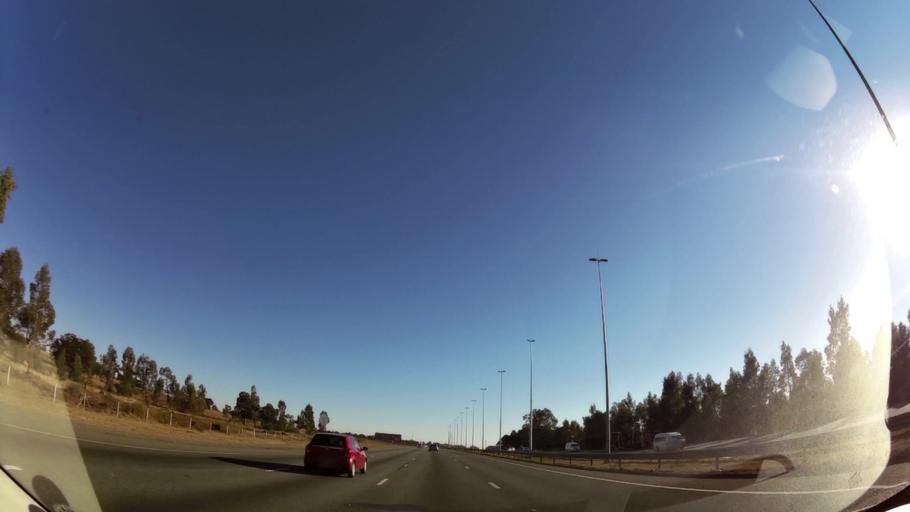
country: ZA
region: Gauteng
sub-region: Ekurhuleni Metropolitan Municipality
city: Tembisa
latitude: -25.9137
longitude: 28.2589
